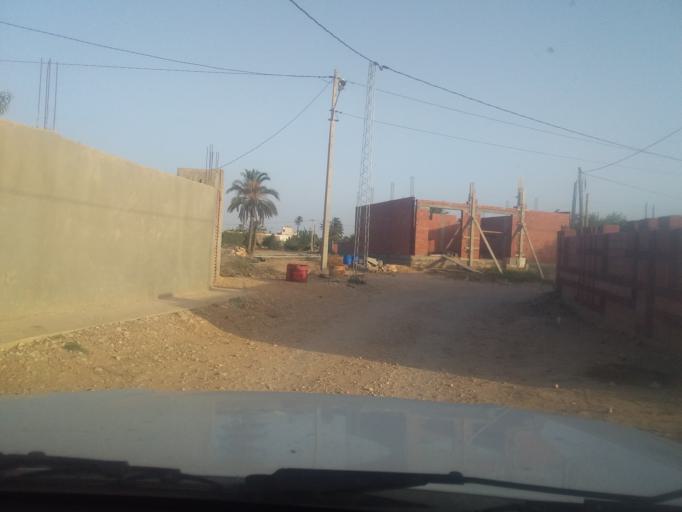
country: TN
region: Qabis
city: Gabes
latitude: 33.6252
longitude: 10.2922
